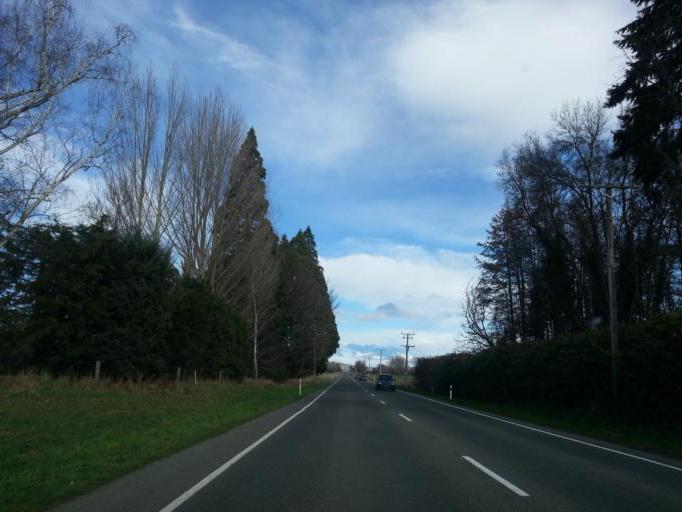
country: NZ
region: Canterbury
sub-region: Hurunui District
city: Amberley
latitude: -42.7920
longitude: 172.8338
